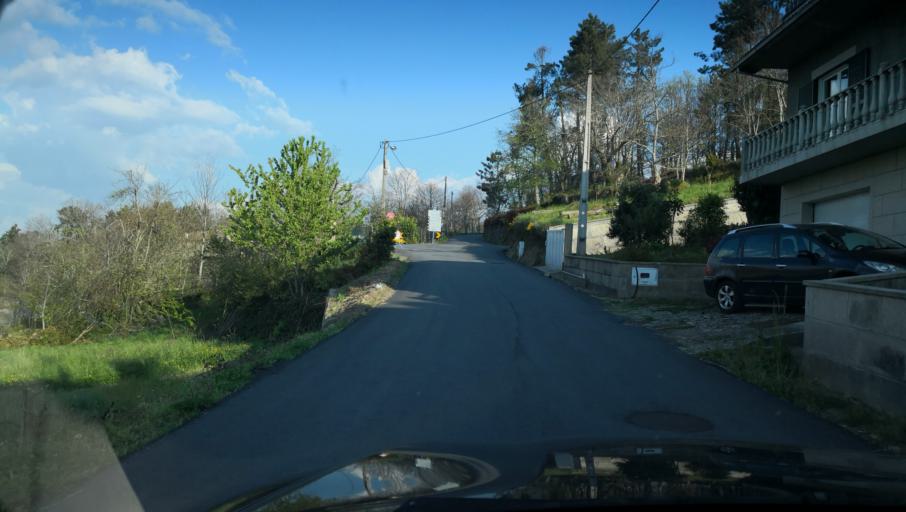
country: PT
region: Vila Real
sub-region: Santa Marta de Penaguiao
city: Santa Marta de Penaguiao
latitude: 41.2776
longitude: -7.8153
